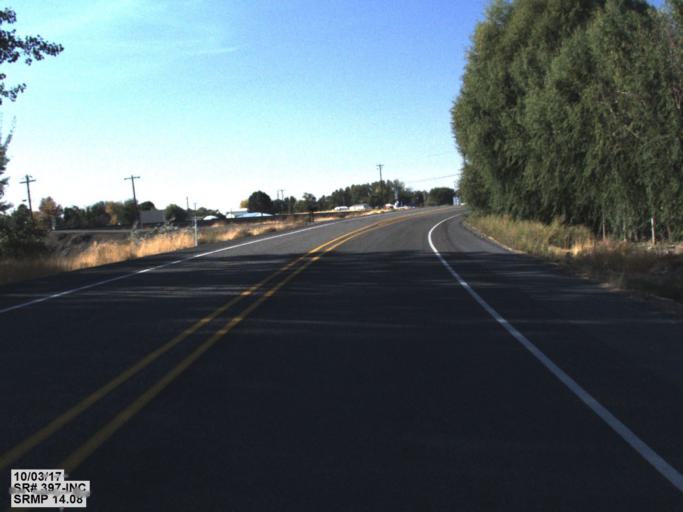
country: US
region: Washington
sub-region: Benton County
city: Finley
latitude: 46.1746
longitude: -119.0582
